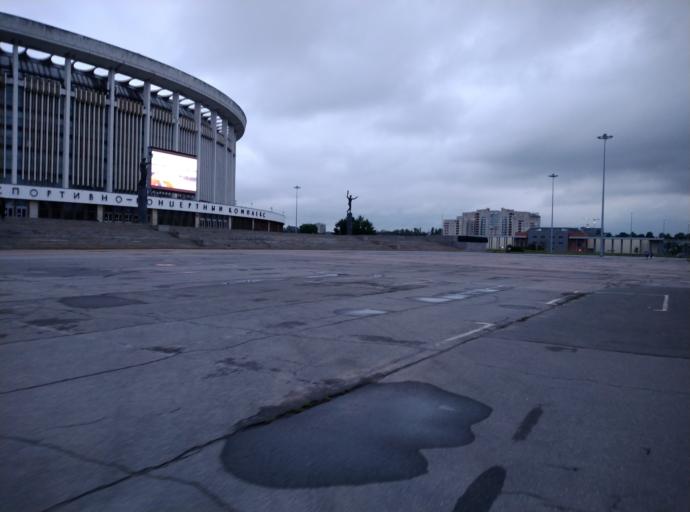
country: RU
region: St.-Petersburg
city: Kupchino
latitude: 59.8699
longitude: 30.3387
